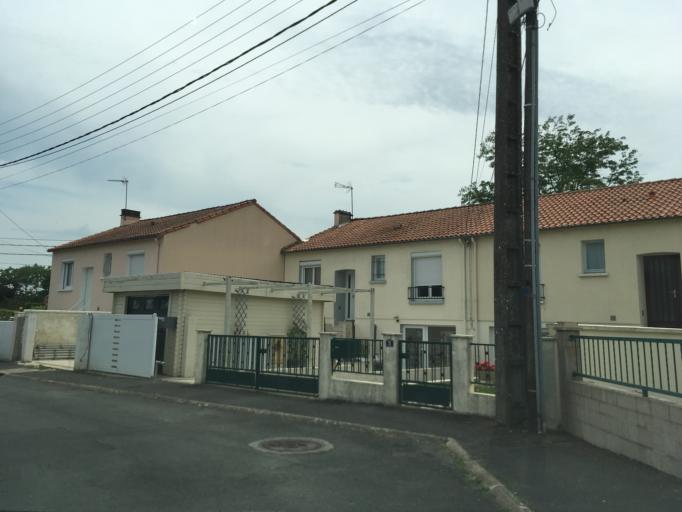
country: FR
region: Poitou-Charentes
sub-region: Departement des Deux-Sevres
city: Niort
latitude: 46.3210
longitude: -0.4882
